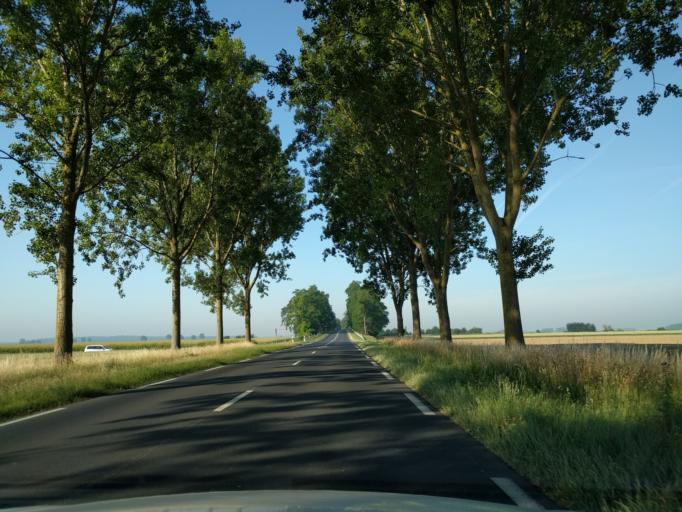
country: FR
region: Picardie
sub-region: Departement de la Somme
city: Chaulnes
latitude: 49.7972
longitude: 2.8398
